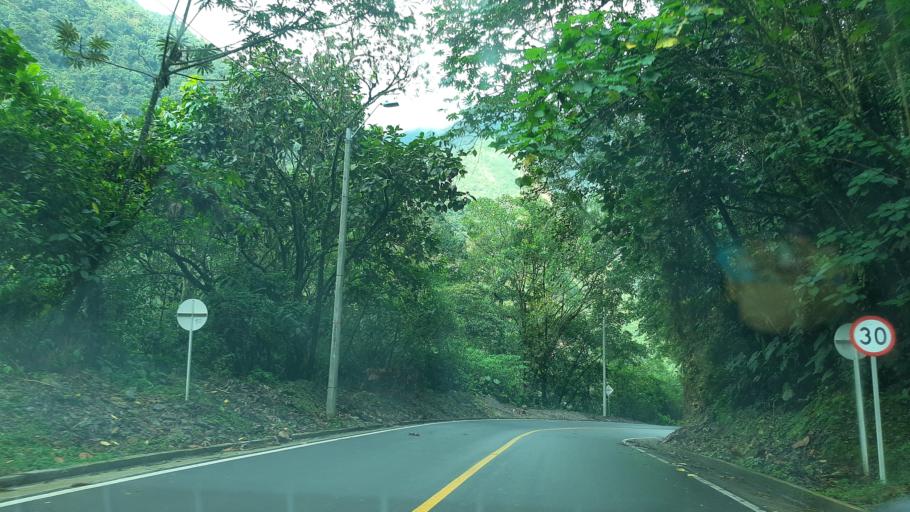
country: CO
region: Boyaca
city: Santa Maria
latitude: 4.8942
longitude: -73.2898
